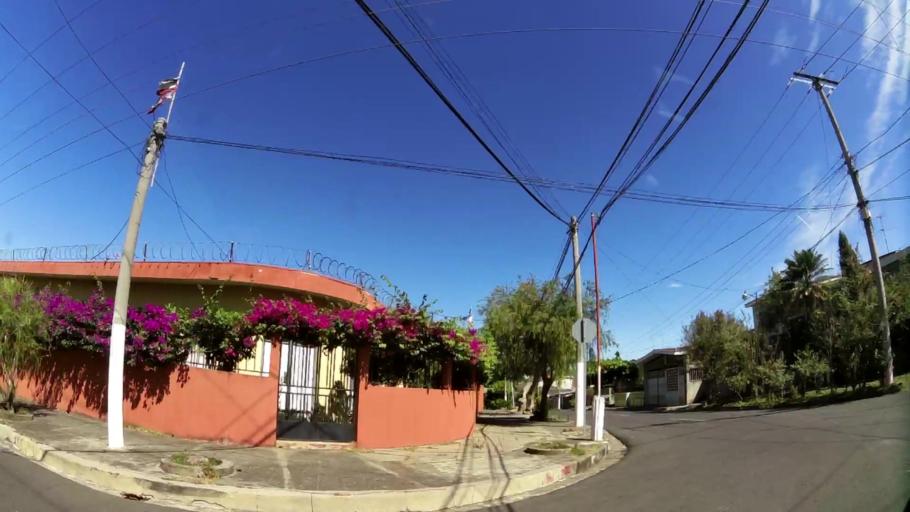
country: SV
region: Ahuachapan
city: Ahuachapan
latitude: 13.9175
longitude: -89.8519
